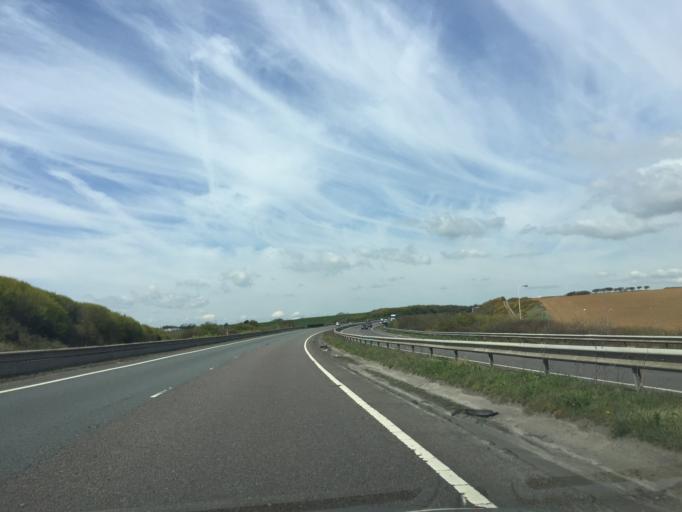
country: GB
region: England
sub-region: Kent
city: Folkestone
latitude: 51.1038
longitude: 1.2436
